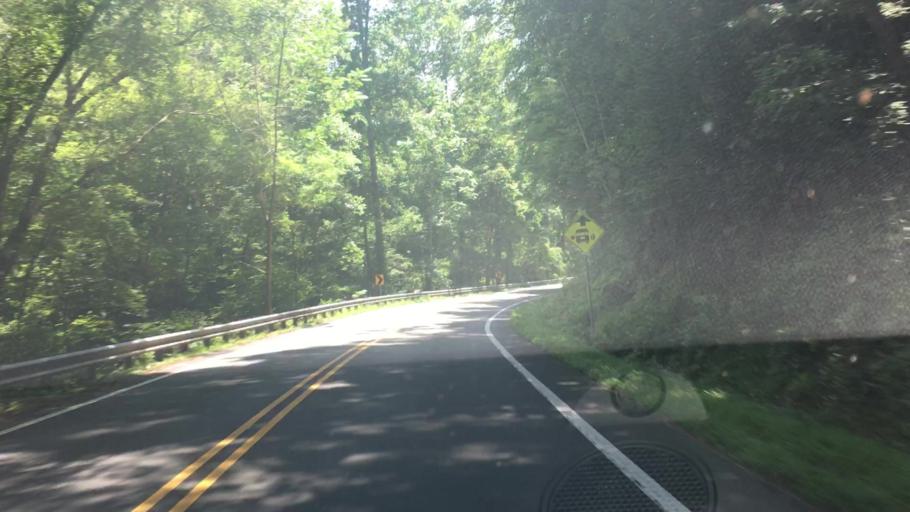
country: US
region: Virginia
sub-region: King George County
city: Passapatanzy
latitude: 38.3030
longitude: -77.2900
